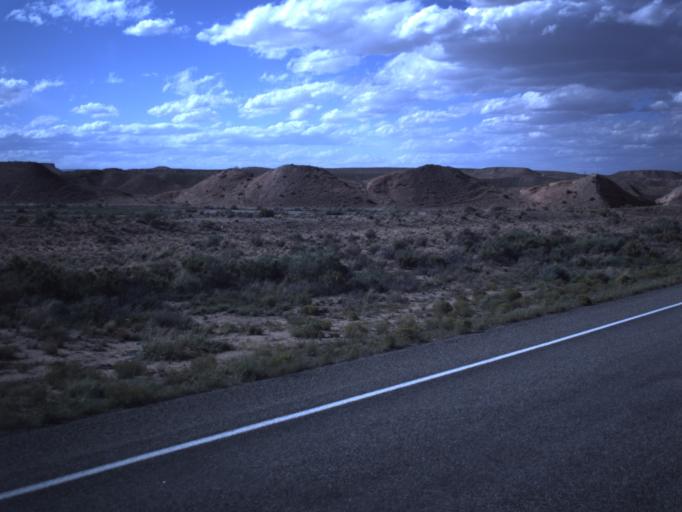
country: US
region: Utah
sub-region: Emery County
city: Ferron
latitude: 38.3206
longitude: -110.6745
